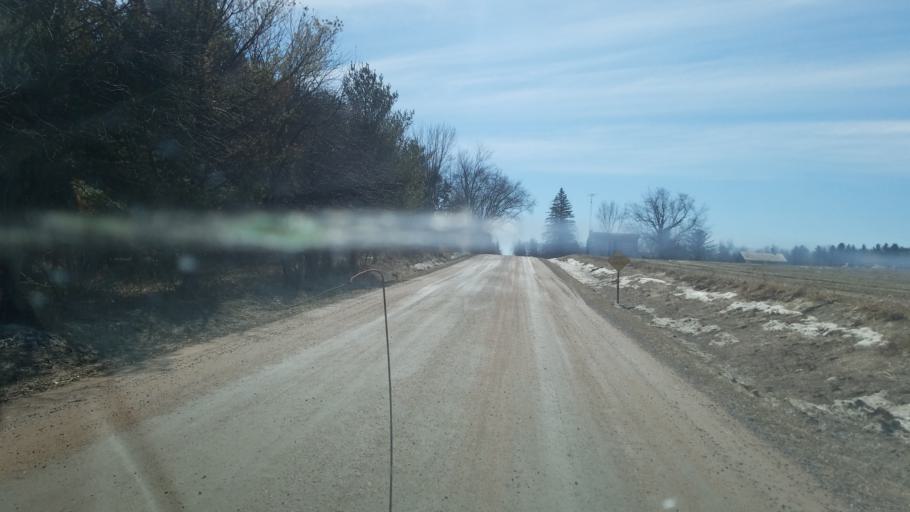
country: US
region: Wisconsin
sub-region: Clark County
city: Neillsville
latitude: 44.5891
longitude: -90.4564
